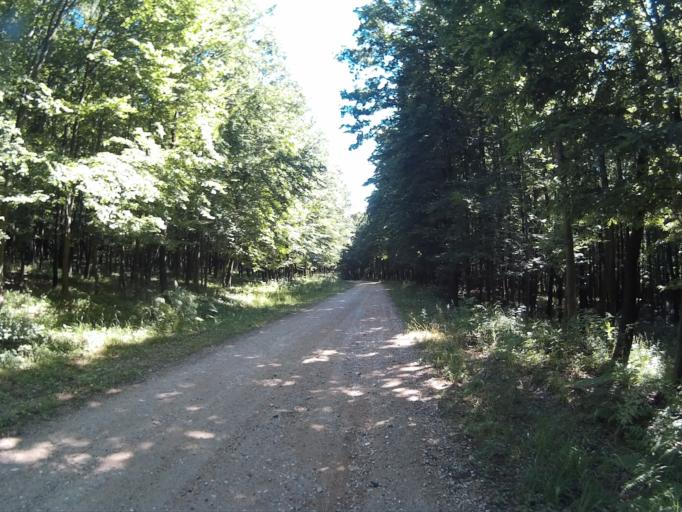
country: HU
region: Veszprem
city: Urkut
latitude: 47.1043
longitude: 17.6659
